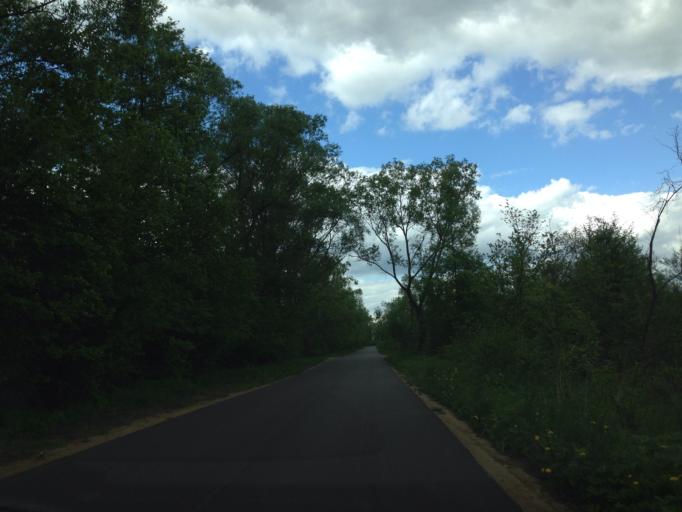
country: PL
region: Podlasie
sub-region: Powiat bialostocki
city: Tykocin
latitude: 53.3138
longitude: 22.6026
